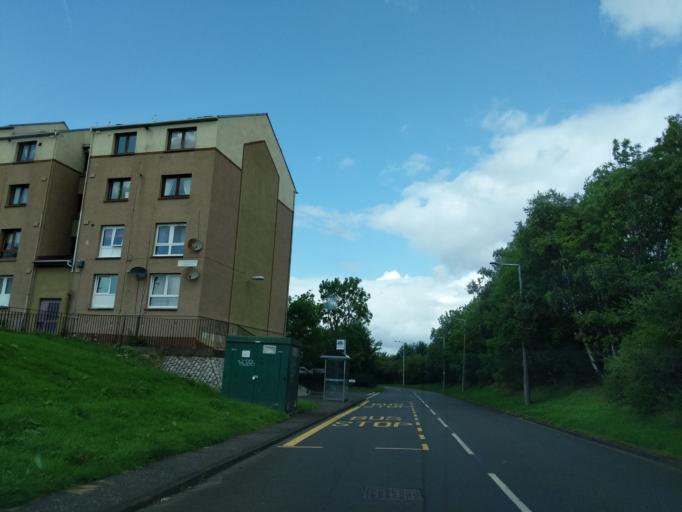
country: GB
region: Scotland
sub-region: Edinburgh
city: Colinton
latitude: 55.9128
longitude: -3.2705
